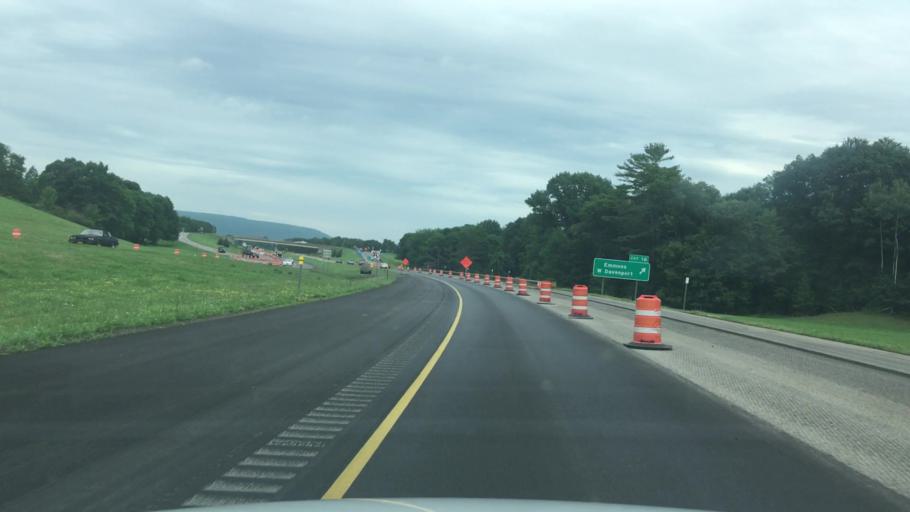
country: US
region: New York
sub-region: Otsego County
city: Oneonta
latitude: 42.4572
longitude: -75.0164
